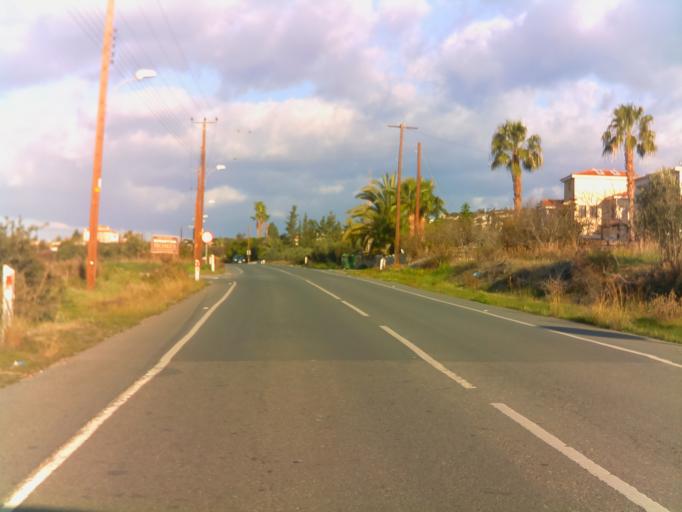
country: CY
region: Pafos
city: Pegeia
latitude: 34.8684
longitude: 32.3652
